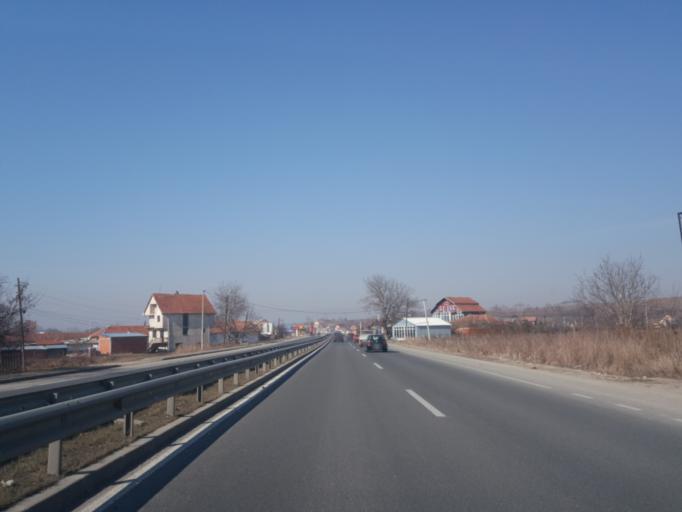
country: XK
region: Pristina
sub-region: Komuna e Obiliqit
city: Obiliq
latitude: 42.7346
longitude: 21.0677
